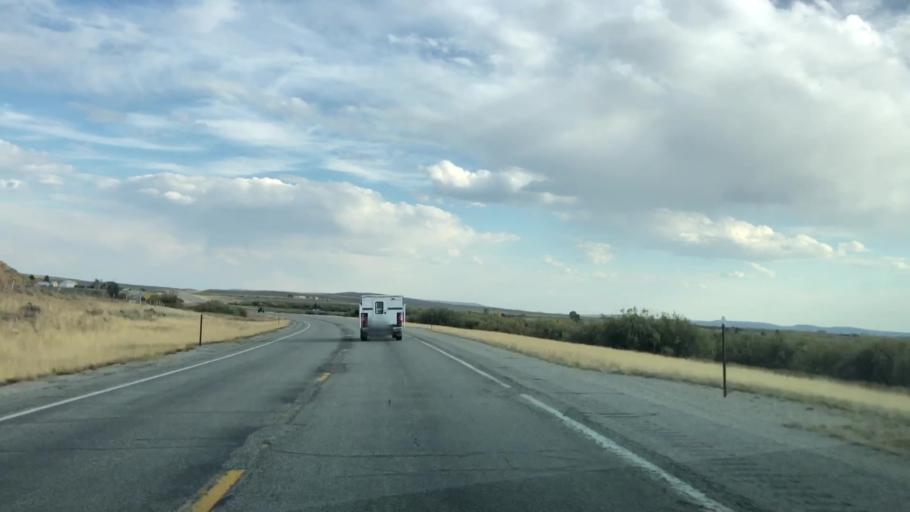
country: US
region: Wyoming
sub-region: Sublette County
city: Pinedale
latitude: 43.0221
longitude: -110.1226
